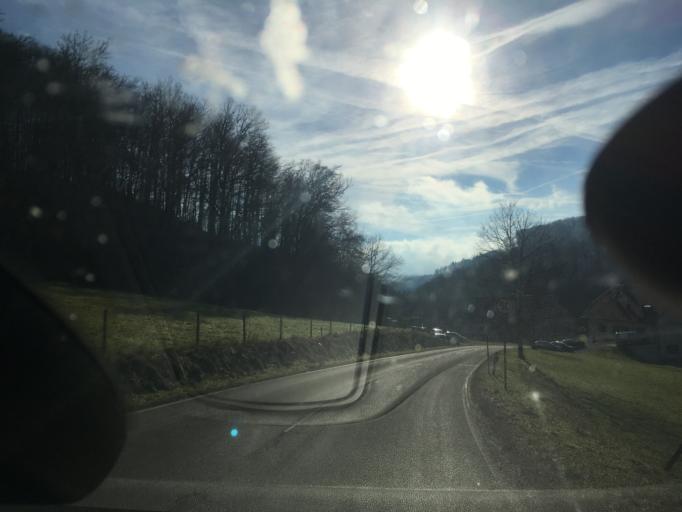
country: DE
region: Baden-Wuerttemberg
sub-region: Freiburg Region
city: Gorwihl
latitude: 47.6288
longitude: 8.0893
